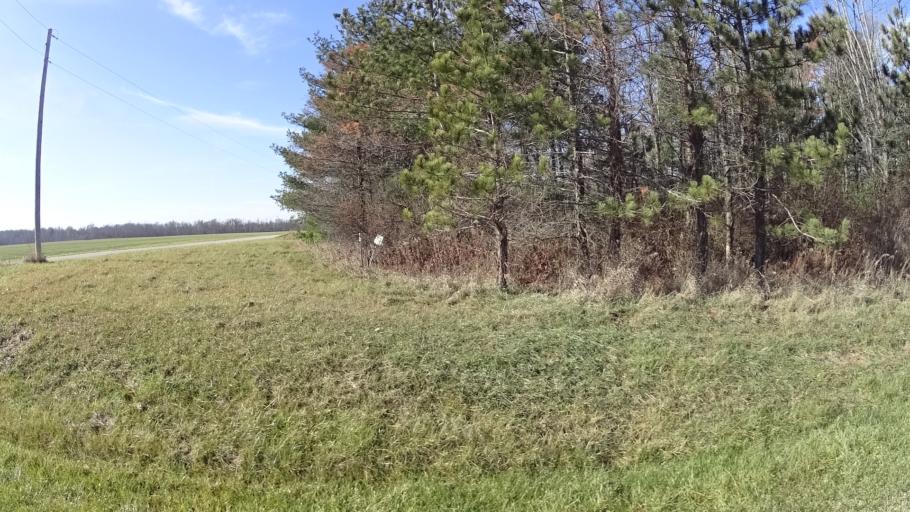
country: US
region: Ohio
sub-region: Lorain County
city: Wellington
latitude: 41.1163
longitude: -82.2004
